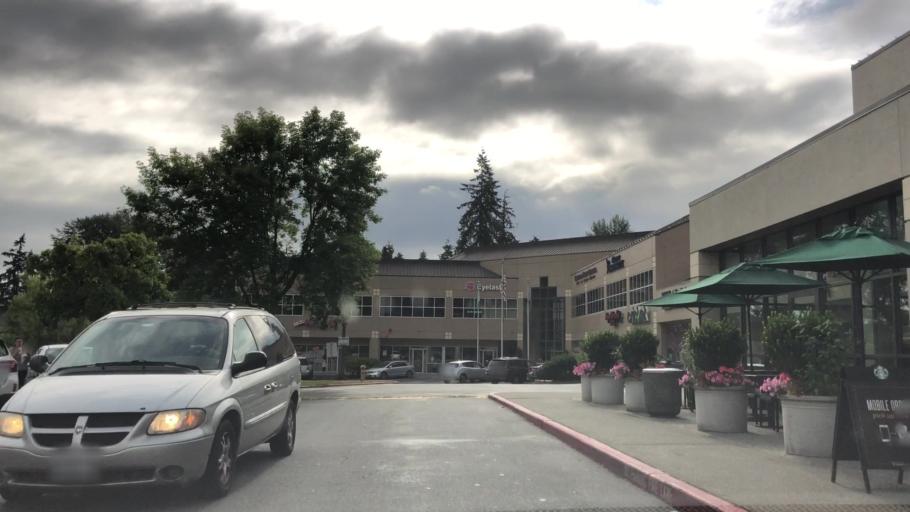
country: US
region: Washington
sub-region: King County
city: Bothell
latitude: 47.7900
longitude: -122.2157
